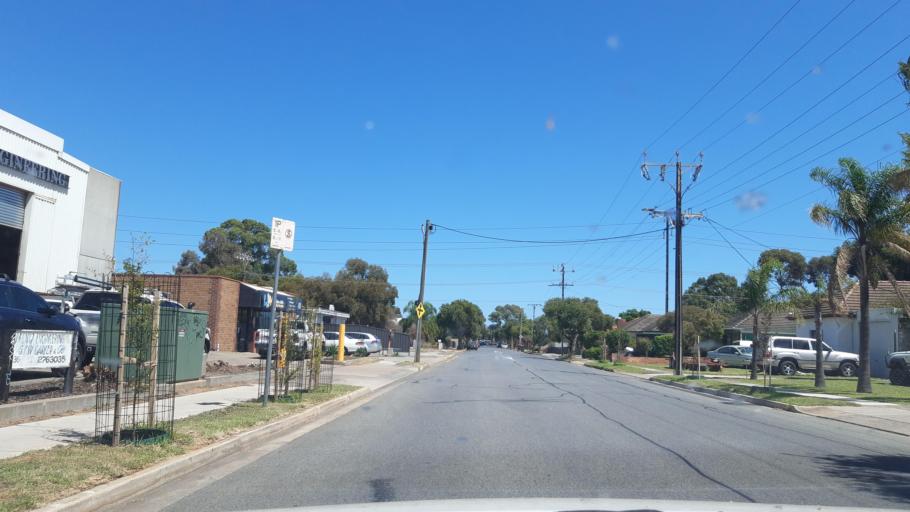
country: AU
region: South Australia
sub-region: Mitcham
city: Clarence Gardens
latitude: -34.9833
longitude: 138.5706
